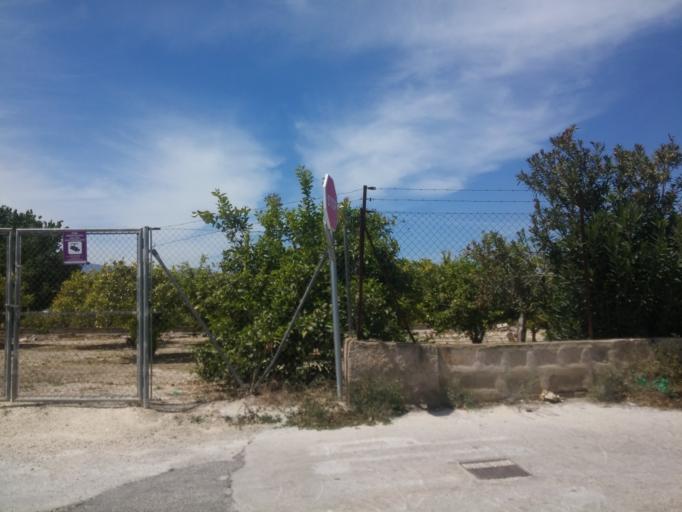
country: ES
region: Valencia
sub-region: Provincia de Alicante
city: Villajoyosa
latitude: 38.5157
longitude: -0.2263
